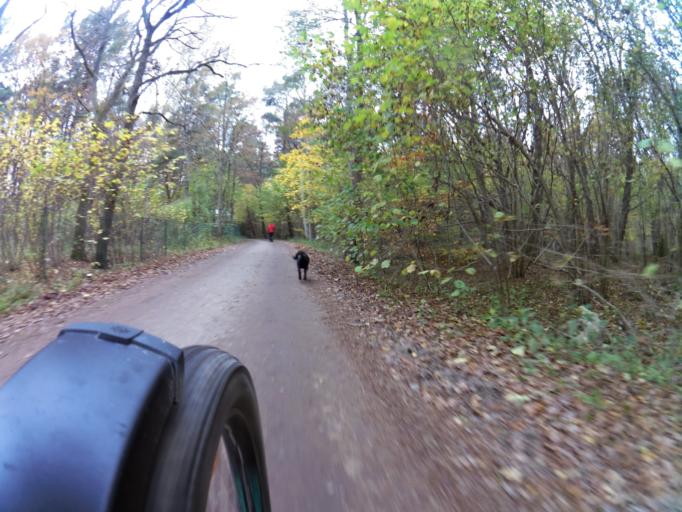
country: PL
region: Pomeranian Voivodeship
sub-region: Powiat pucki
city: Krokowa
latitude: 54.8289
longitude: 18.0985
